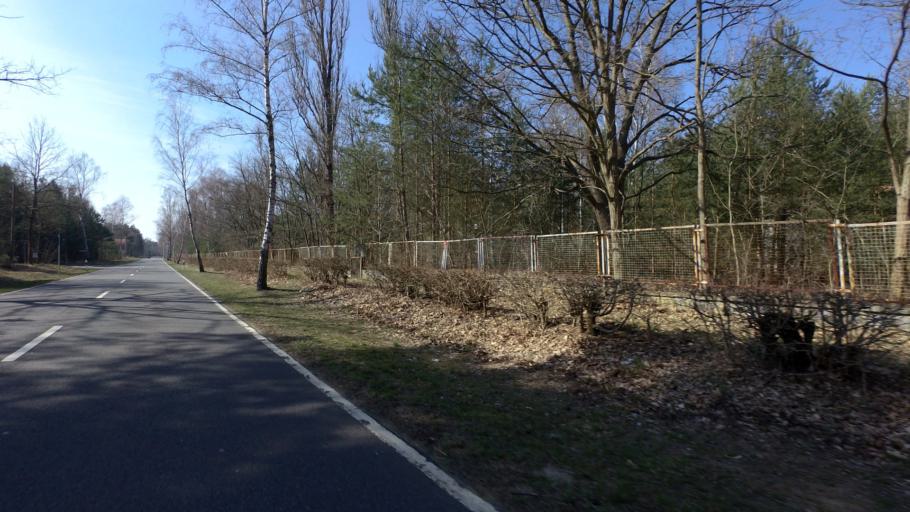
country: DE
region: Brandenburg
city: Sperenberg
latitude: 52.0966
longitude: 13.3656
